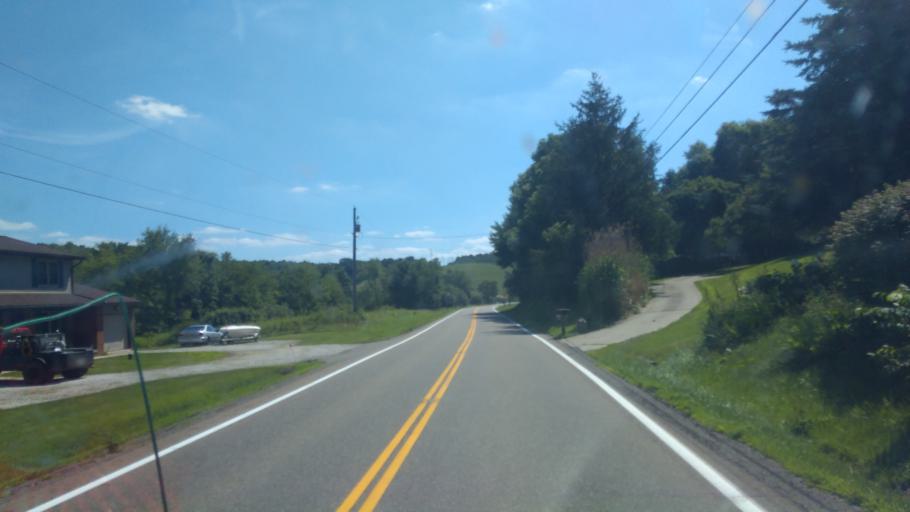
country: US
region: Ohio
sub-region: Carroll County
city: Carrollton
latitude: 40.5790
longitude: -81.1098
